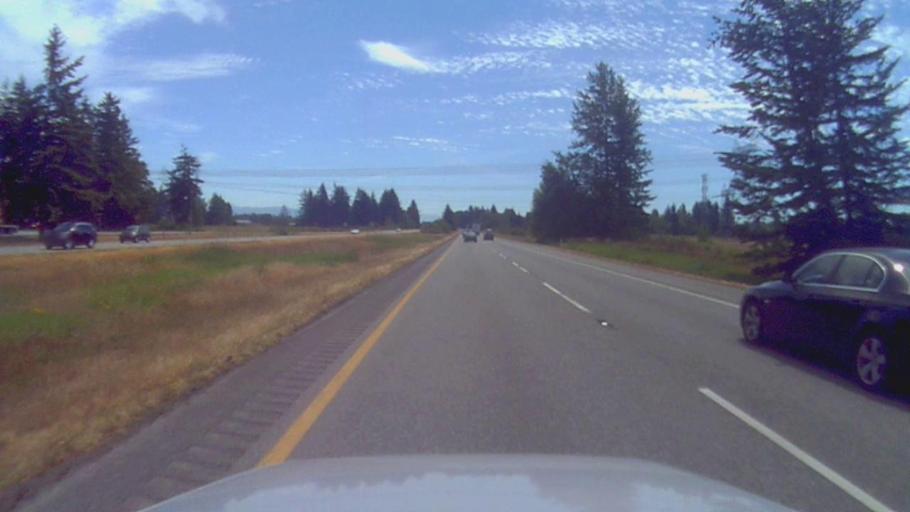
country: US
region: Washington
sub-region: Whatcom County
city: Ferndale
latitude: 48.9088
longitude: -122.6238
